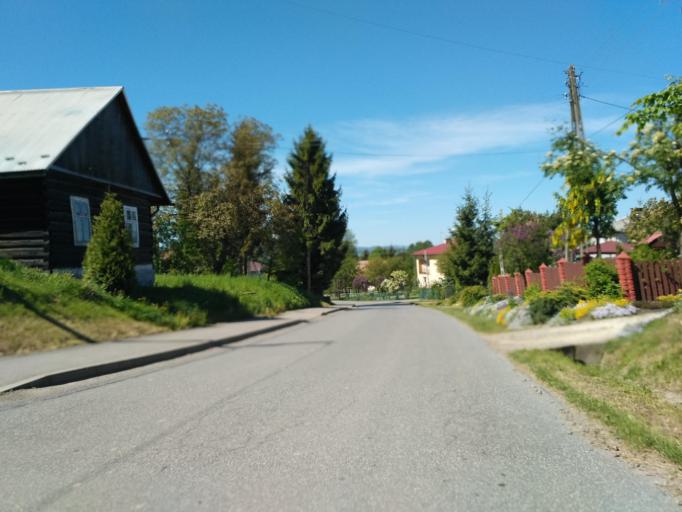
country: PL
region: Subcarpathian Voivodeship
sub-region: Powiat brzozowski
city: Turze Pole
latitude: 49.6394
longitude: 21.9978
